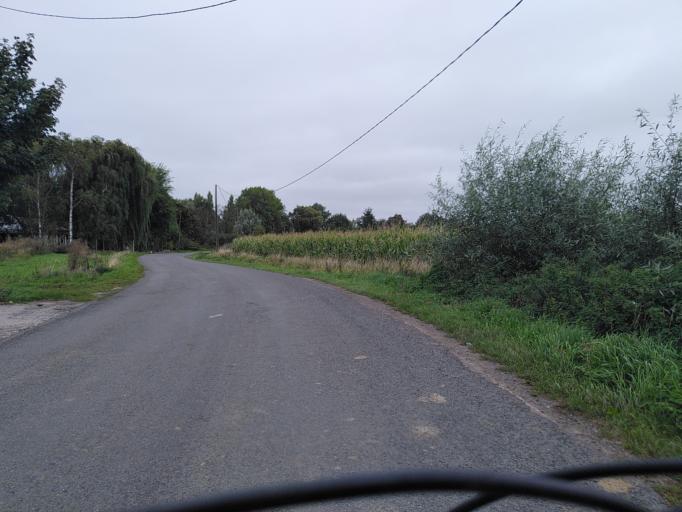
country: FR
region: Nord-Pas-de-Calais
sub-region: Departement du Pas-de-Calais
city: Laventie
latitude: 50.6380
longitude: 2.8018
